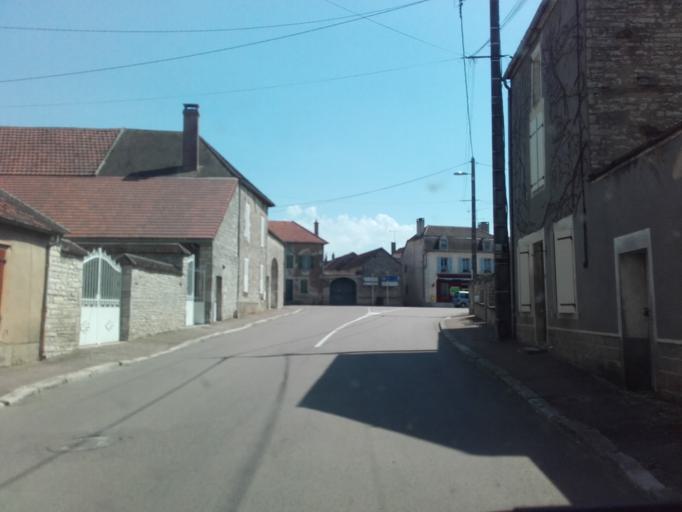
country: FR
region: Bourgogne
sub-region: Departement de l'Yonne
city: Joux-la-Ville
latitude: 47.6735
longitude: 3.8782
